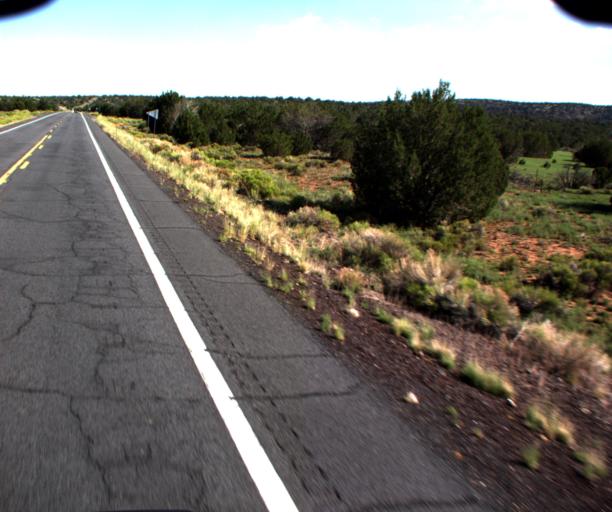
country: US
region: Arizona
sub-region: Coconino County
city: Williams
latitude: 35.4584
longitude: -112.1708
